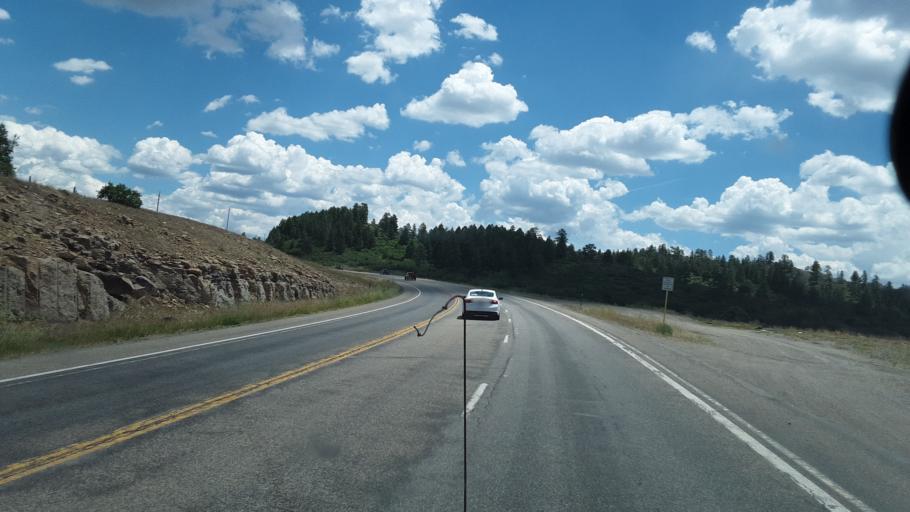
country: US
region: Colorado
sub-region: Archuleta County
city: Pagosa Springs
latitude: 37.2275
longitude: -107.1188
